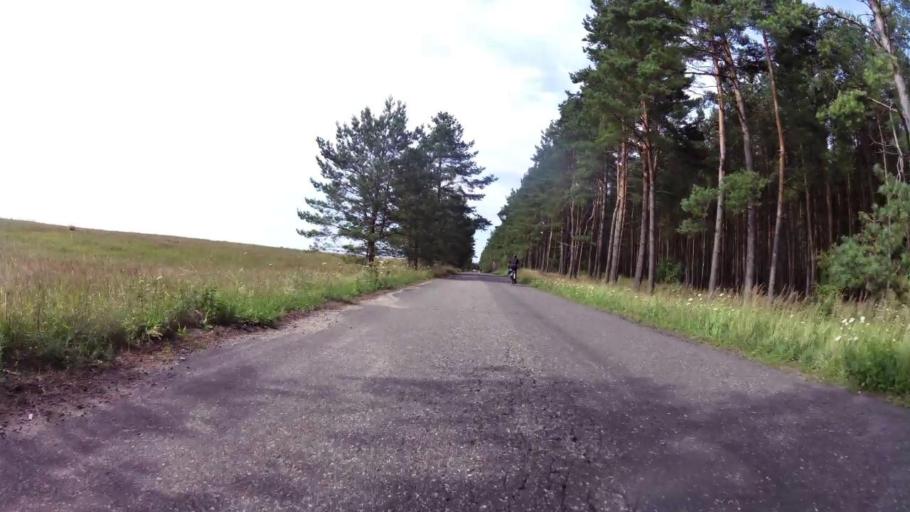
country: PL
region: West Pomeranian Voivodeship
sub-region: Powiat stargardzki
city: Insko
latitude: 53.3907
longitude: 15.5954
